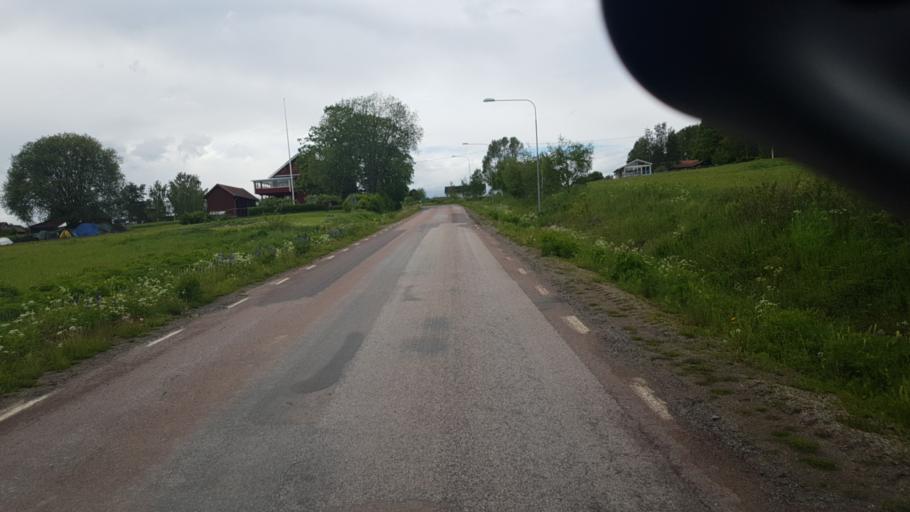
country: SE
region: Vaermland
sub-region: Eda Kommun
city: Charlottenberg
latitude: 59.8294
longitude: 12.3383
